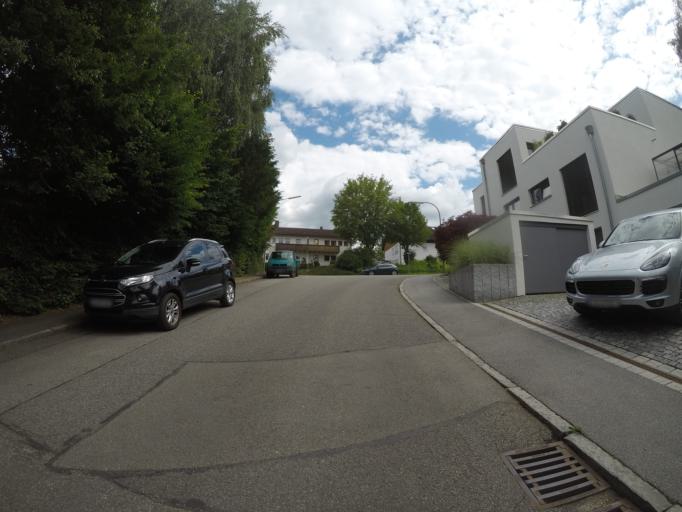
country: DE
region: Bavaria
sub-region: Lower Bavaria
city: Landshut
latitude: 48.5170
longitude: 12.1442
